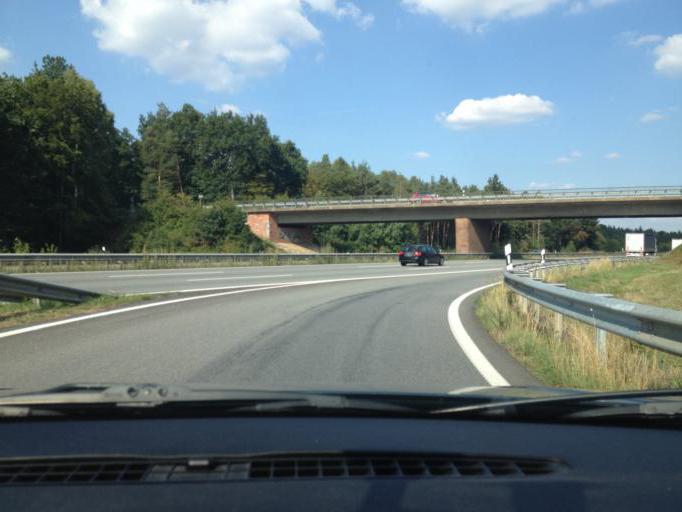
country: DE
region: Rheinland-Pfalz
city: Rodenbach
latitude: 49.4406
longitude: 7.6513
